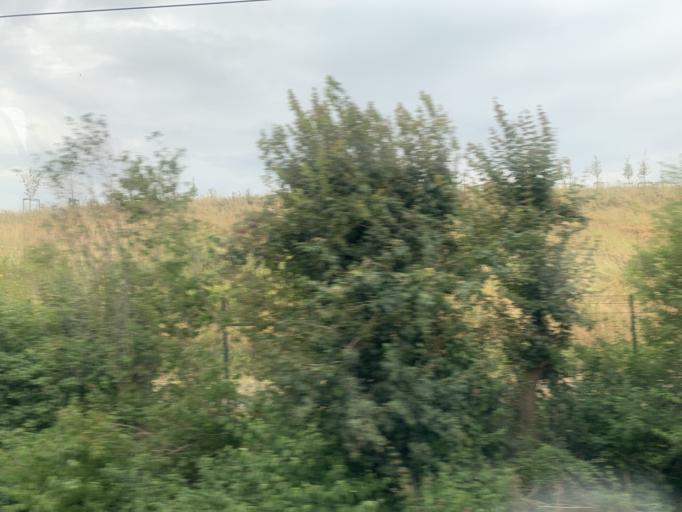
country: DE
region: North Rhine-Westphalia
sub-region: Regierungsbezirk Koln
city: Kerpen
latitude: 50.8813
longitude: 6.6233
